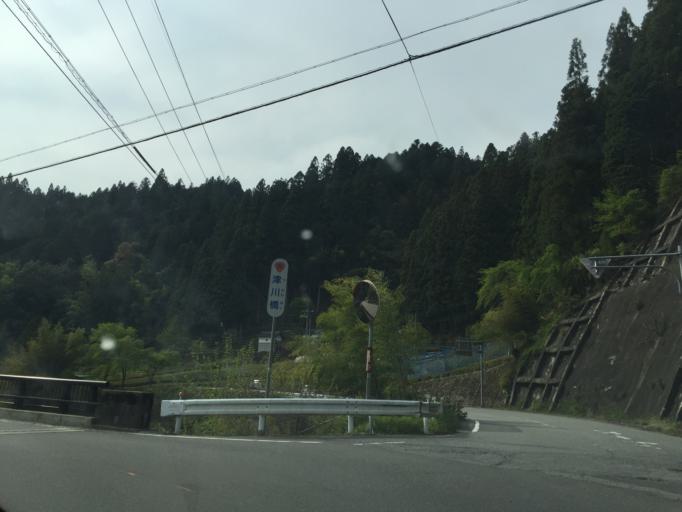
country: JP
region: Aichi
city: Shinshiro
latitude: 35.1379
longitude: 137.6932
